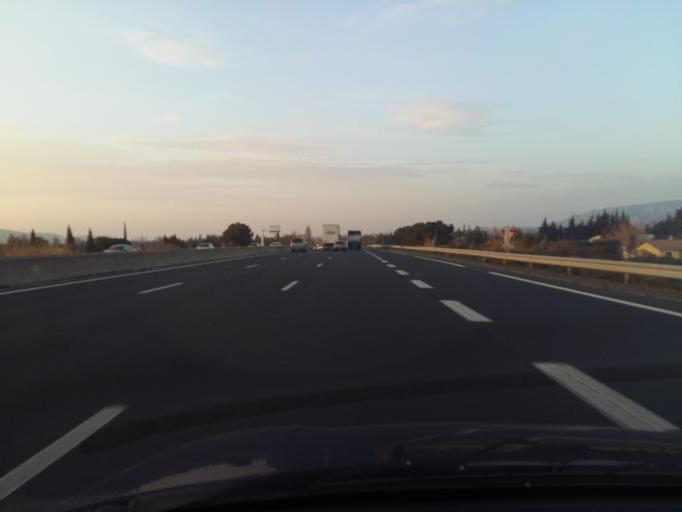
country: FR
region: Provence-Alpes-Cote d'Azur
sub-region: Departement des Bouches-du-Rhone
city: Senas
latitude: 43.7463
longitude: 5.0861
